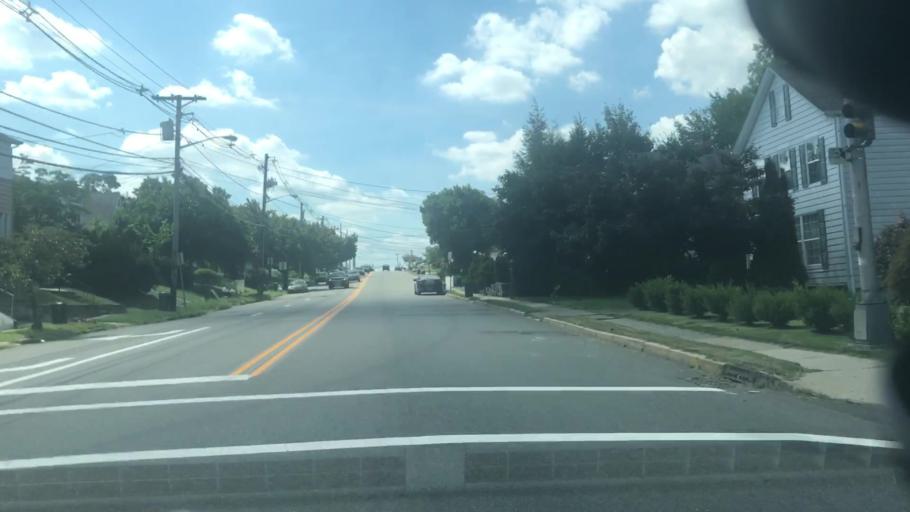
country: US
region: New Jersey
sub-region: Essex County
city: Bloomfield
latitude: 40.8064
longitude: -74.1679
